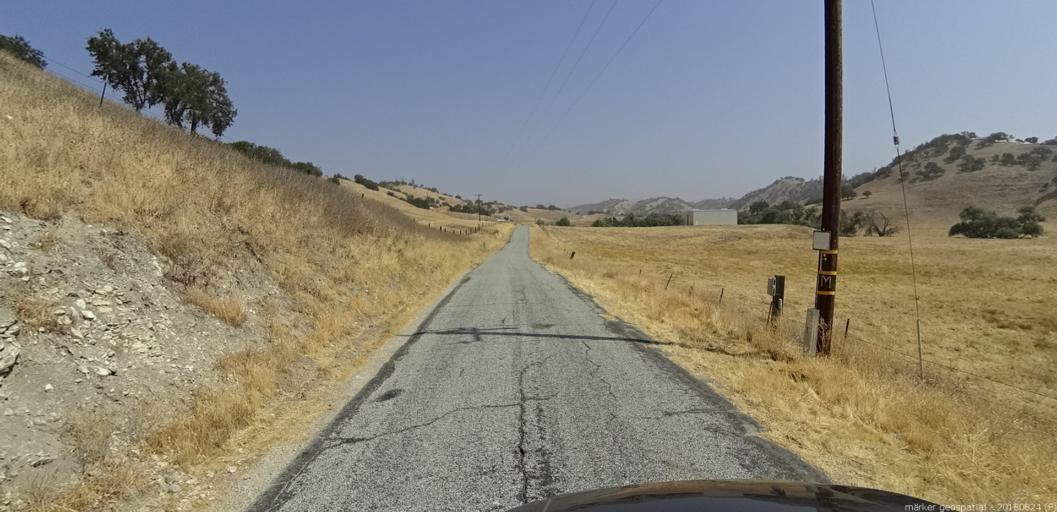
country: US
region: California
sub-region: San Luis Obispo County
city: San Miguel
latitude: 35.9636
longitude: -120.6523
